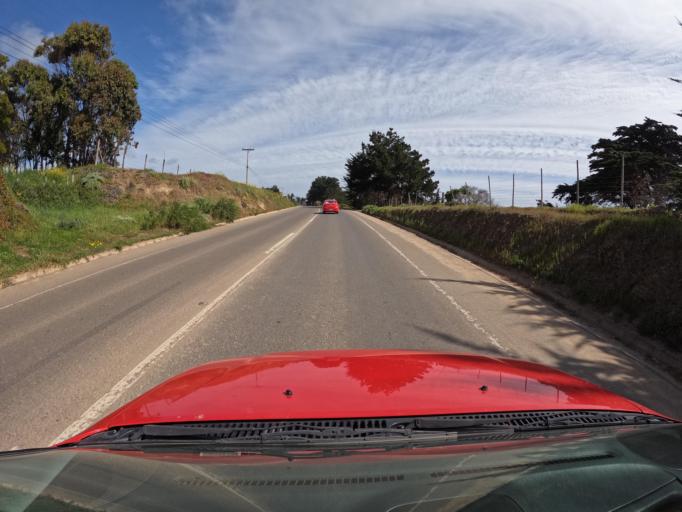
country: CL
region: O'Higgins
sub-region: Provincia de Colchagua
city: Santa Cruz
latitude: -34.4209
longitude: -72.0308
